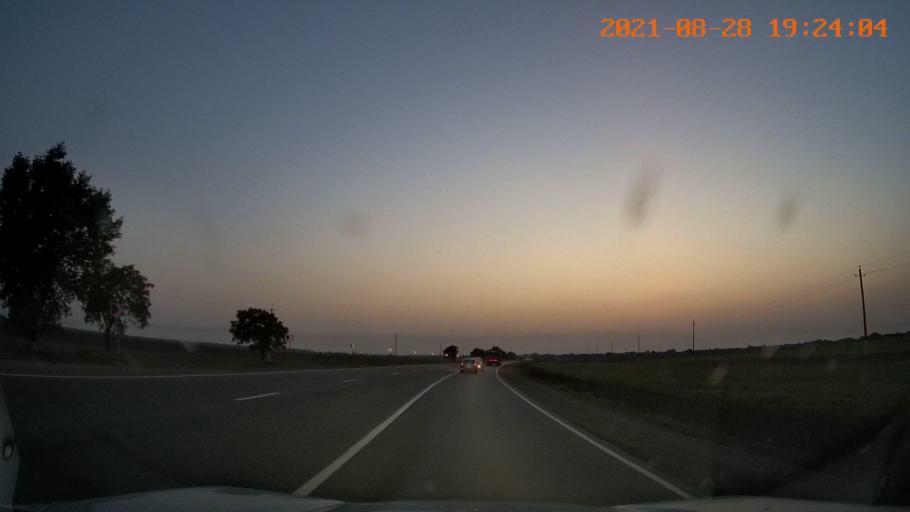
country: RU
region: Adygeya
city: Ponezhukay
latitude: 44.8729
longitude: 39.4392
